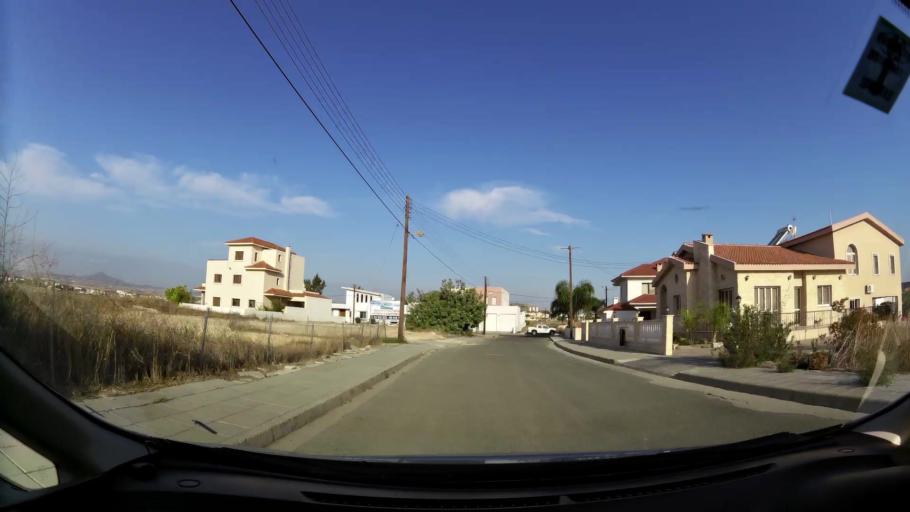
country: CY
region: Larnaka
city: Aradippou
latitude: 34.9296
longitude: 33.5961
